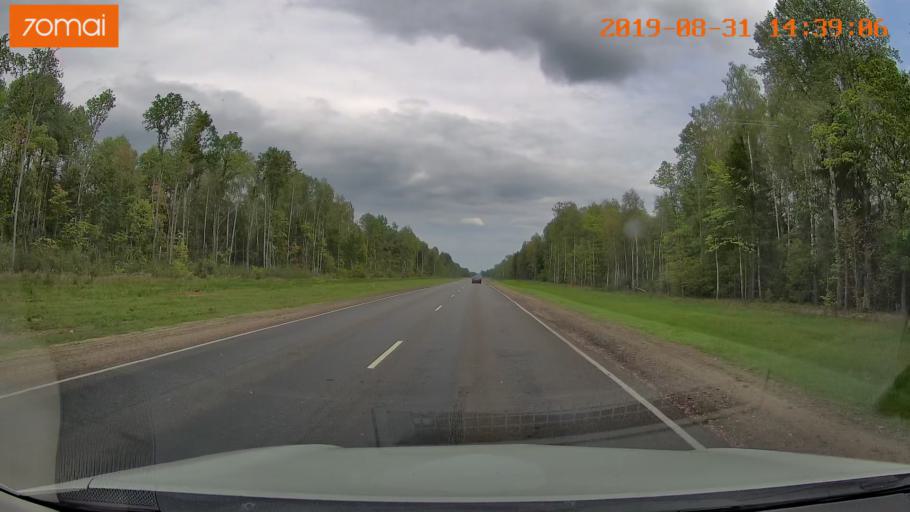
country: RU
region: Smolensk
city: Yekimovichi
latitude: 54.1892
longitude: 33.5443
